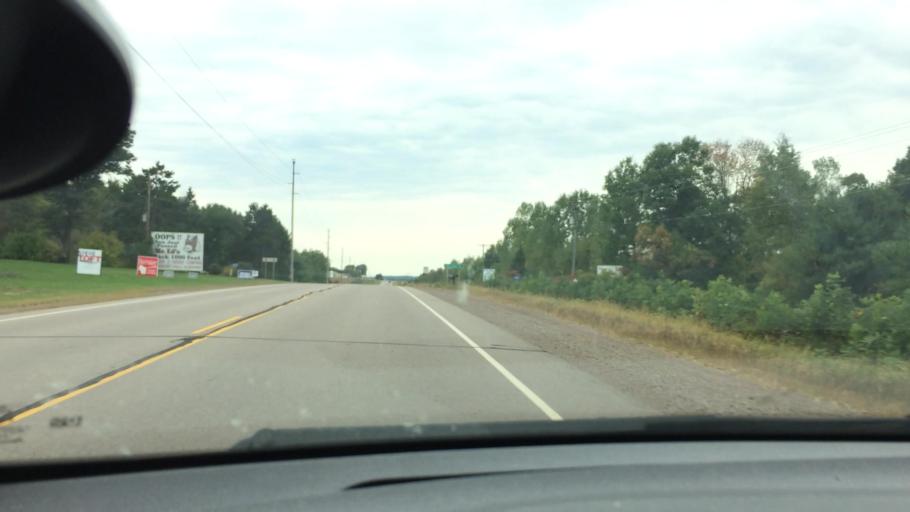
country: US
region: Wisconsin
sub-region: Eau Claire County
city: Augusta
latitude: 44.5963
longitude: -90.9212
